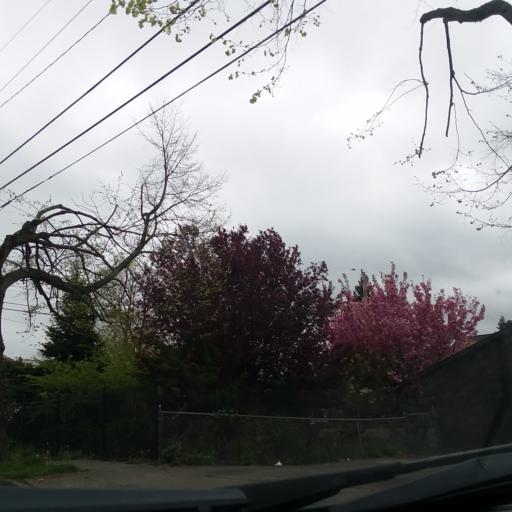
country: US
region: Washington
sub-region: King County
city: White Center
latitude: 47.5067
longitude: -122.3368
